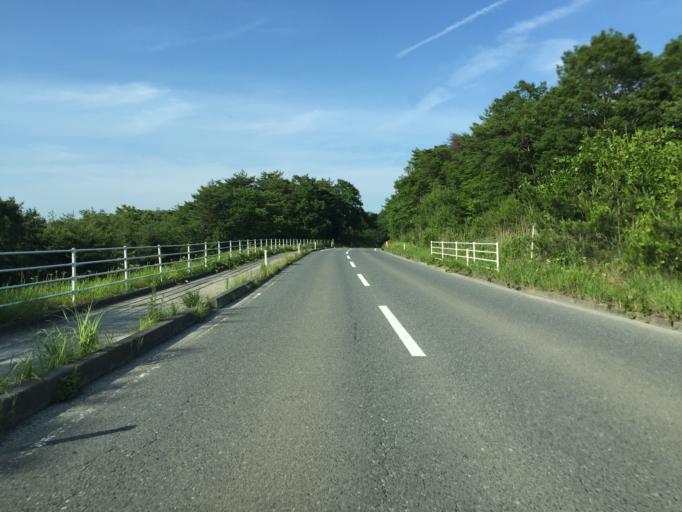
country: JP
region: Fukushima
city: Namie
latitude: 37.6669
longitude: 140.9769
